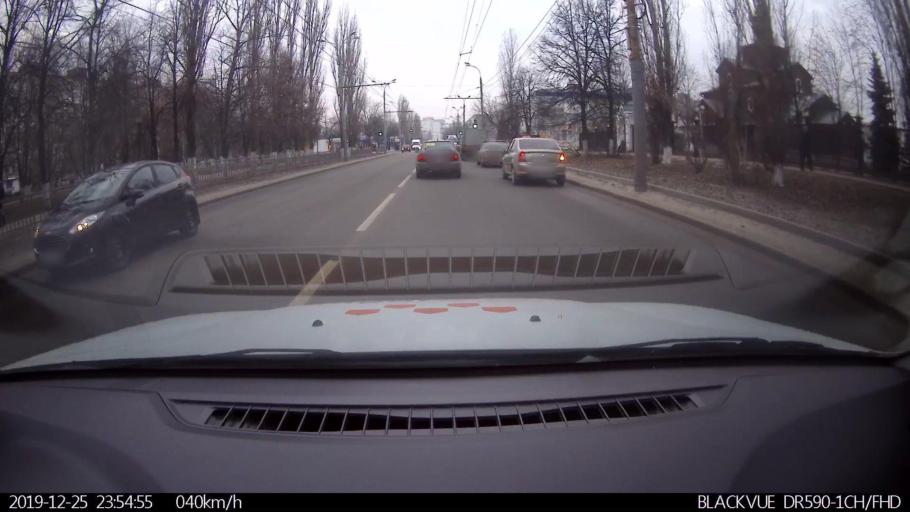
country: RU
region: Nizjnij Novgorod
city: Gorbatovka
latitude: 56.2619
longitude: 43.8797
